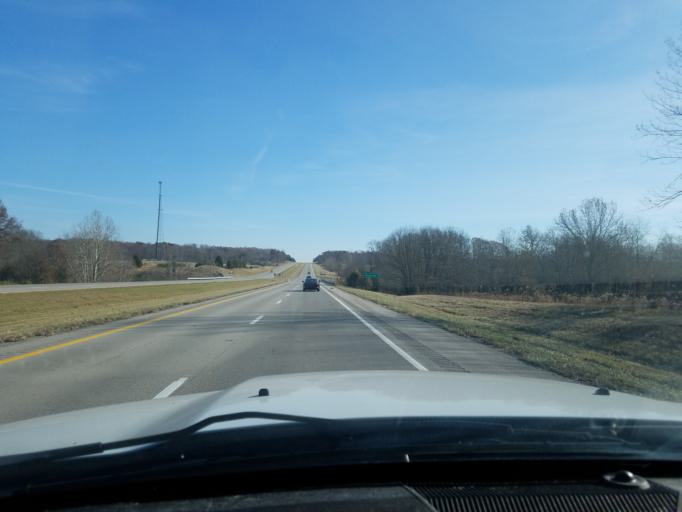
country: US
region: Ohio
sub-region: Adams County
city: Winchester
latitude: 38.9339
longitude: -83.6231
